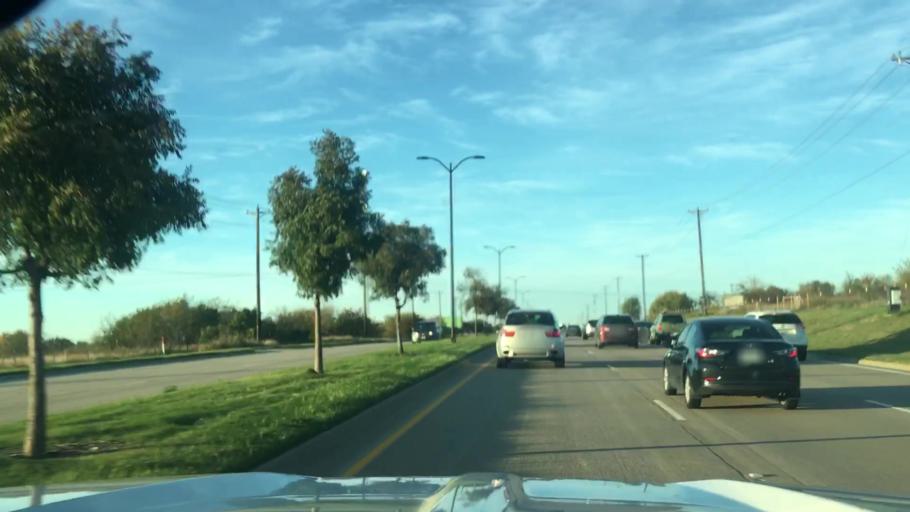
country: US
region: Texas
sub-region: Collin County
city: Prosper
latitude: 33.1984
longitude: -96.8027
